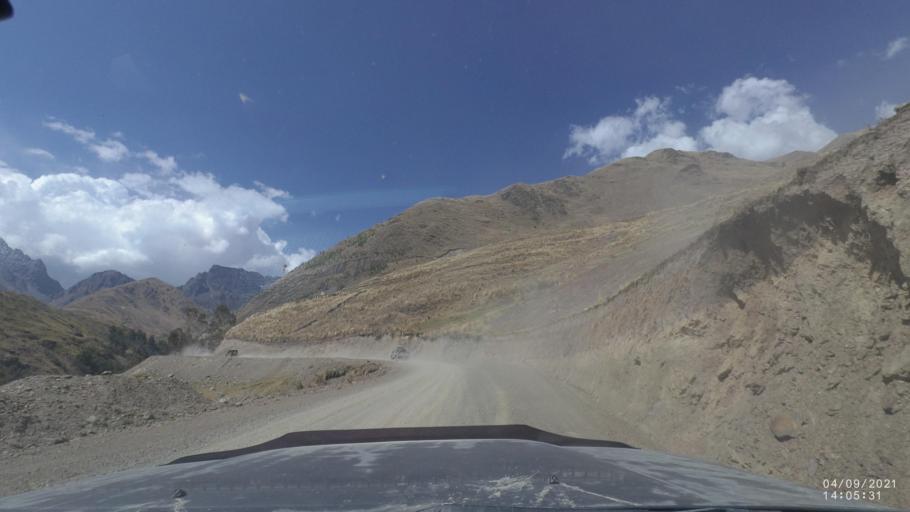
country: BO
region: Cochabamba
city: Sipe Sipe
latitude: -17.2332
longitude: -66.4751
